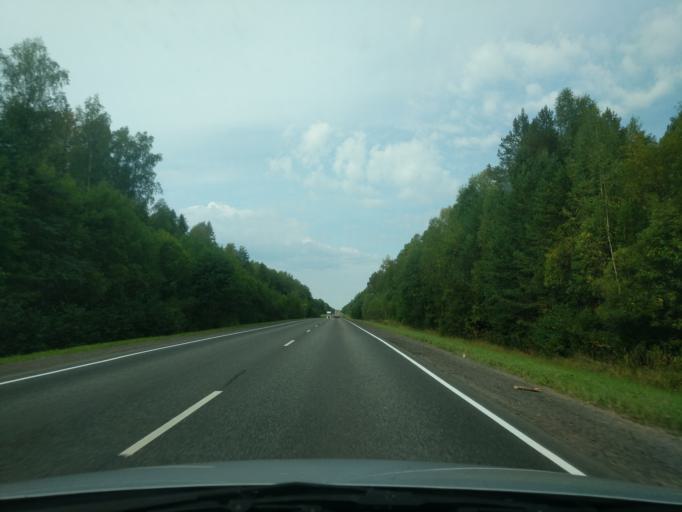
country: RU
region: Kirov
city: Leninskoye
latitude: 58.3188
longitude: 46.8886
